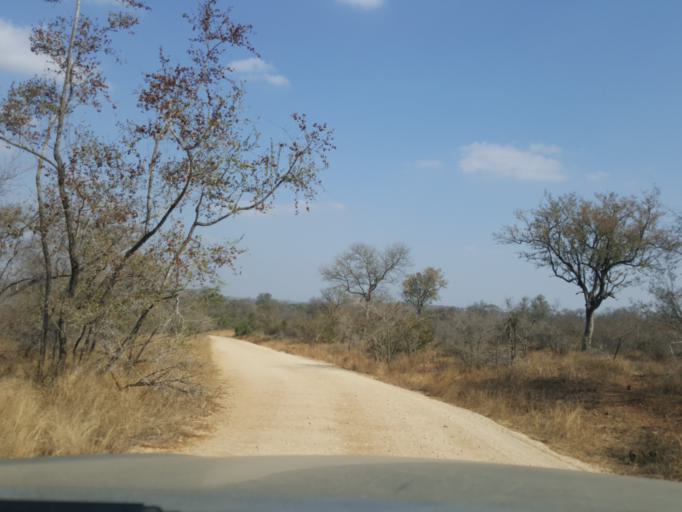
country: ZA
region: Mpumalanga
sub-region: Ehlanzeni District
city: Komatipoort
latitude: -25.2840
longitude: 31.7701
